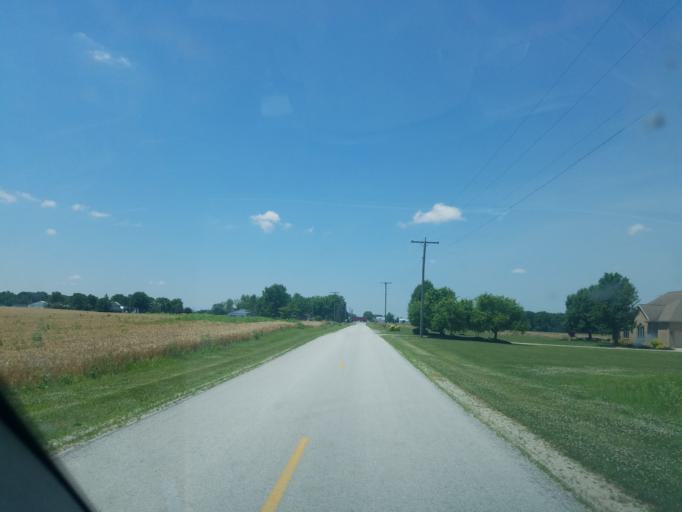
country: US
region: Ohio
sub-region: Hardin County
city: Kenton
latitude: 40.7315
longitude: -83.6227
